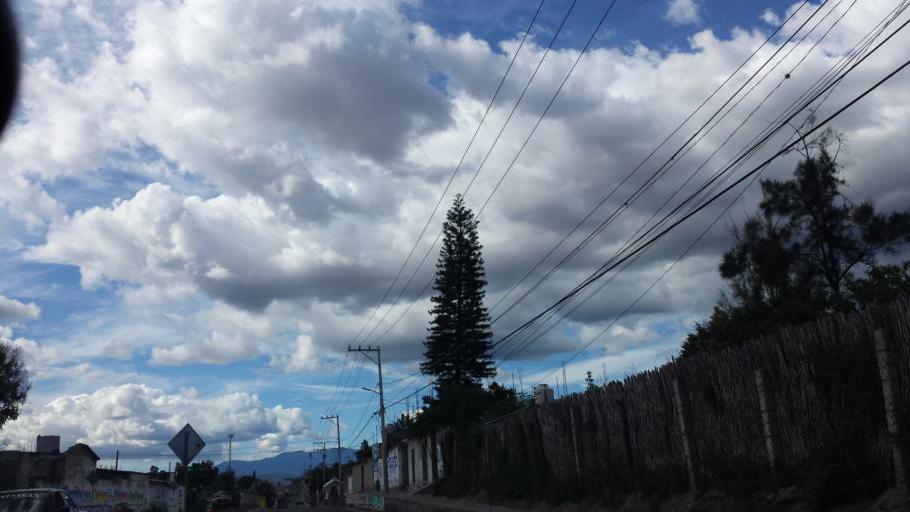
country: MX
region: Oaxaca
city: Tlacolula de Matamoros
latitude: 16.9539
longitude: -96.4696
